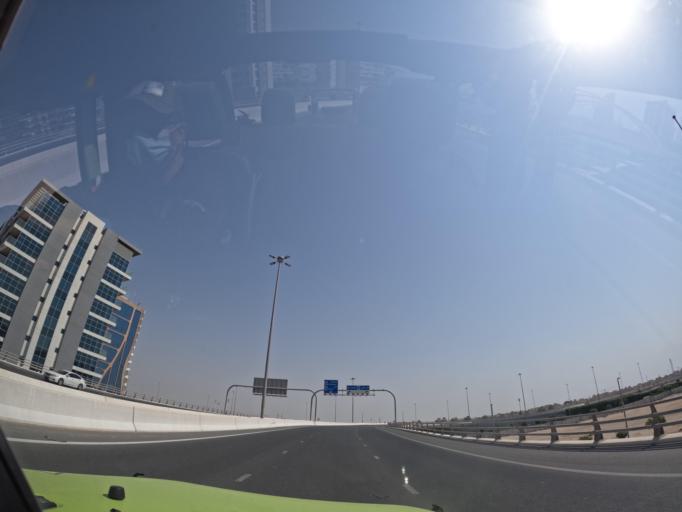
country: AE
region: Abu Dhabi
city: Abu Dhabi
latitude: 24.4429
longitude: 54.5849
